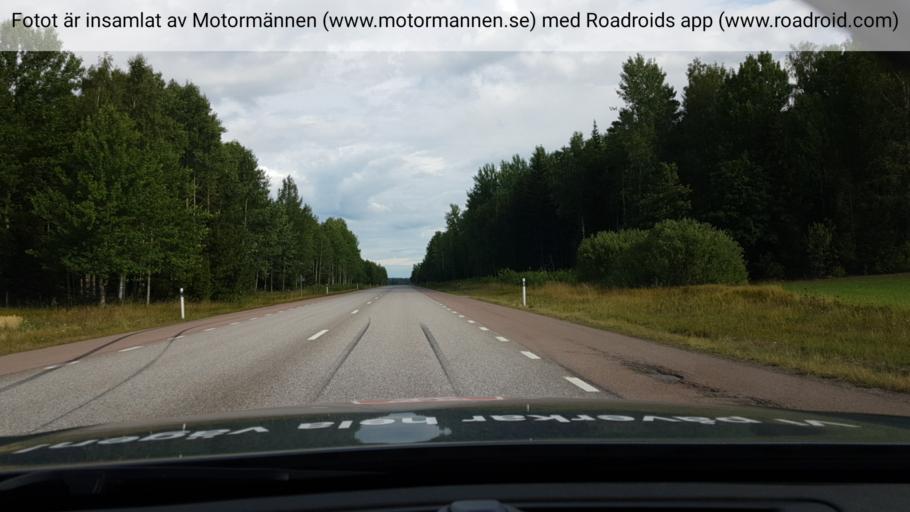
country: SE
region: Uppsala
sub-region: Heby Kommun
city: Morgongava
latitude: 59.8655
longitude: 16.9263
